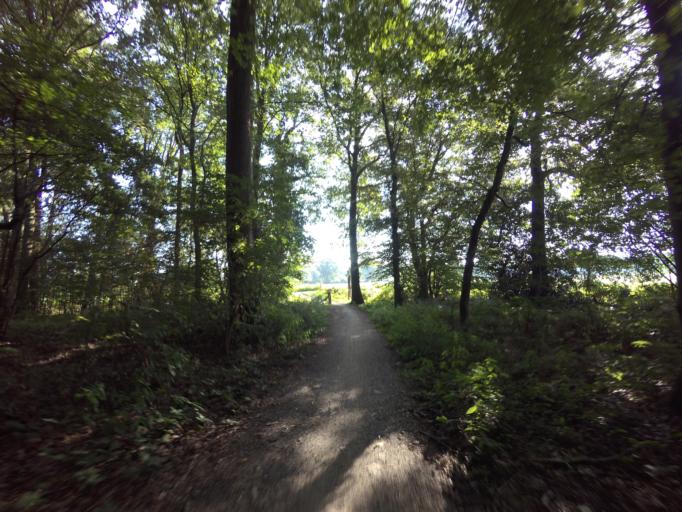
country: NL
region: Gelderland
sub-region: Oude IJsselstreek
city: Wisch
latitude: 51.9230
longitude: 6.4327
